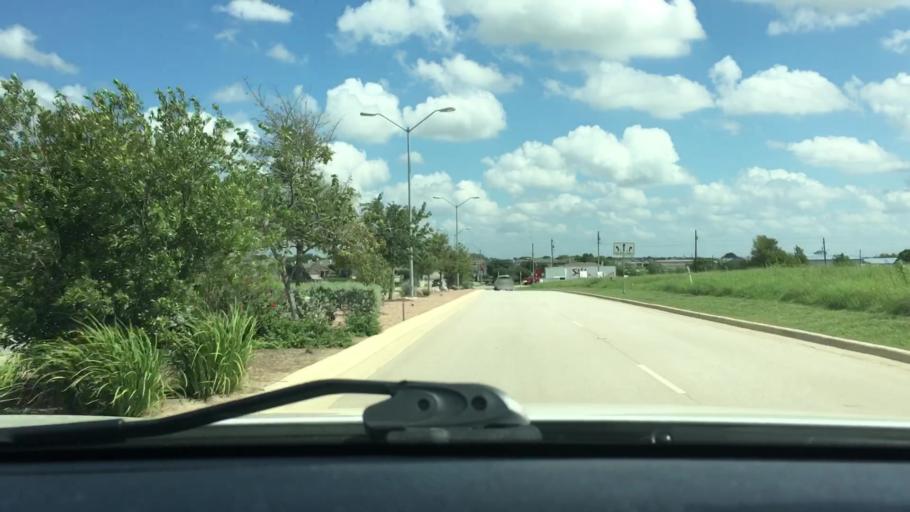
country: US
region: Texas
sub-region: Williamson County
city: Round Rock
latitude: 30.5513
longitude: -97.6786
